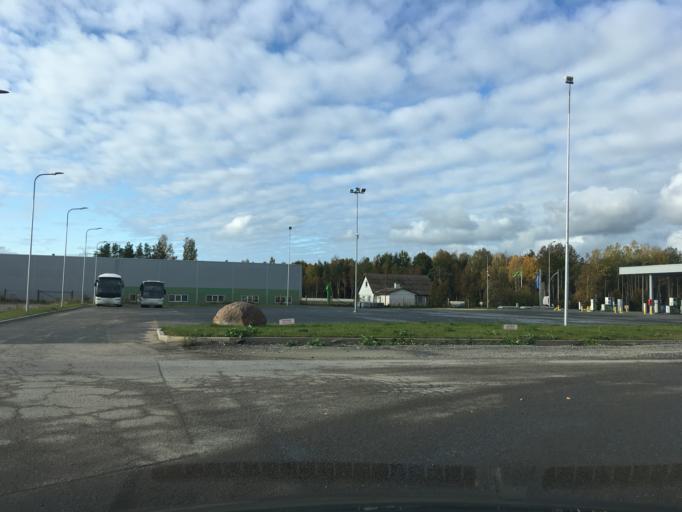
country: EE
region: Harju
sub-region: Joelaehtme vald
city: Loo
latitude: 59.4021
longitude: 24.9189
